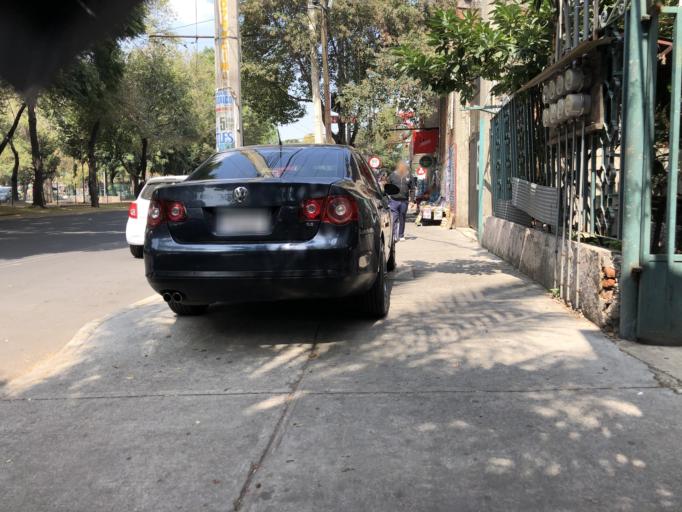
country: MX
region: Mexico City
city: Azcapotzalco
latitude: 19.4736
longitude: -99.1808
